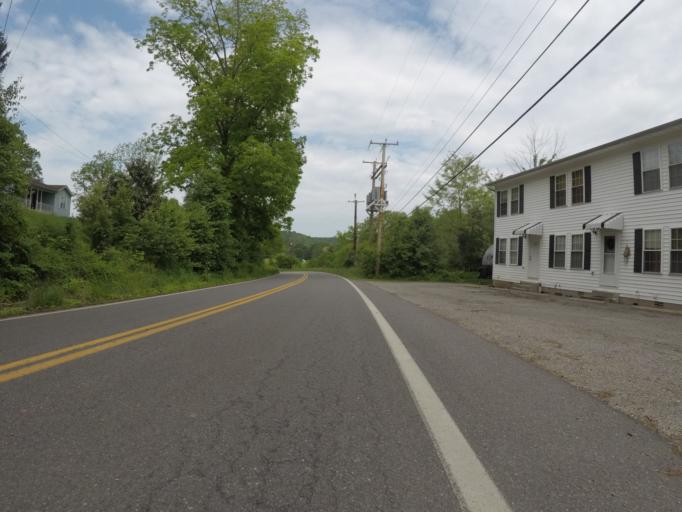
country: US
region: Ohio
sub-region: Lawrence County
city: Burlington
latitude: 38.3569
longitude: -82.5252
